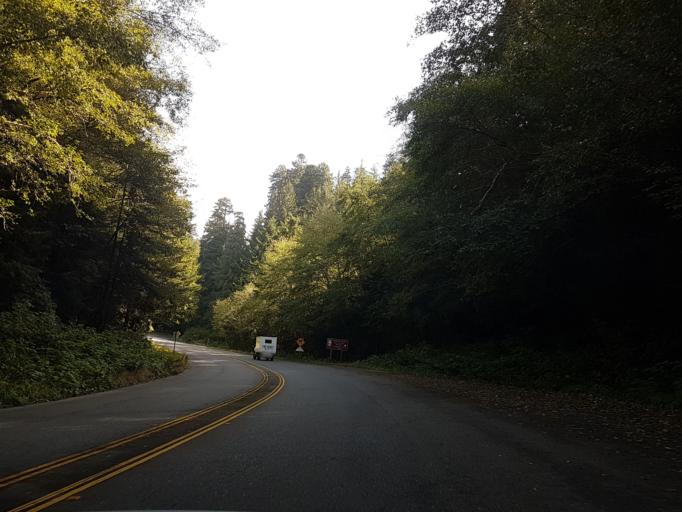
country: US
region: California
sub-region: Del Norte County
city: Bertsch-Oceanview
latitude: 41.4586
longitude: -124.0471
